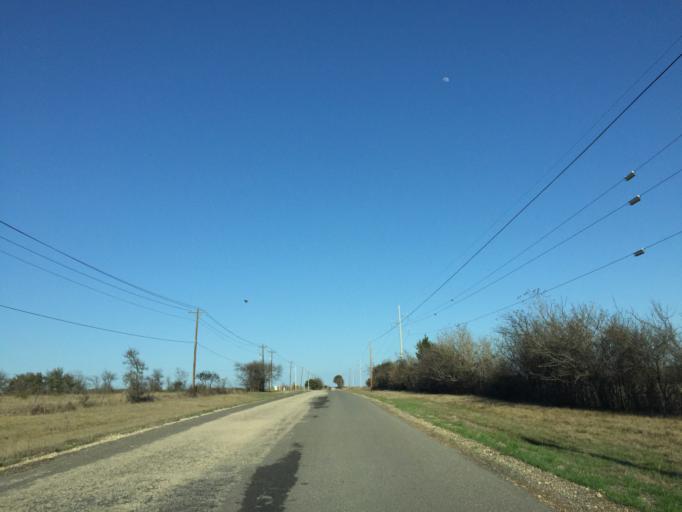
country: US
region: Texas
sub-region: Williamson County
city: Florence
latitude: 30.7799
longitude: -97.7944
